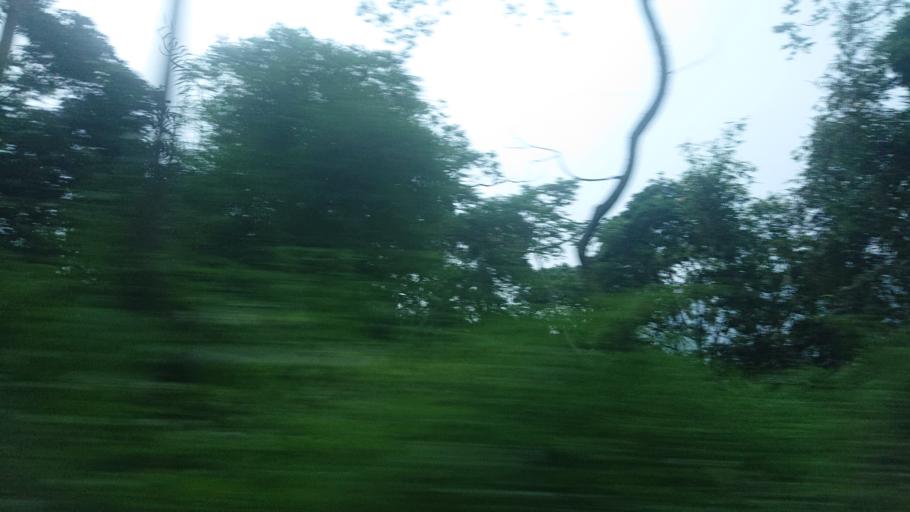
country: TW
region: Taiwan
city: Lugu
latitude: 23.5909
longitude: 120.7239
